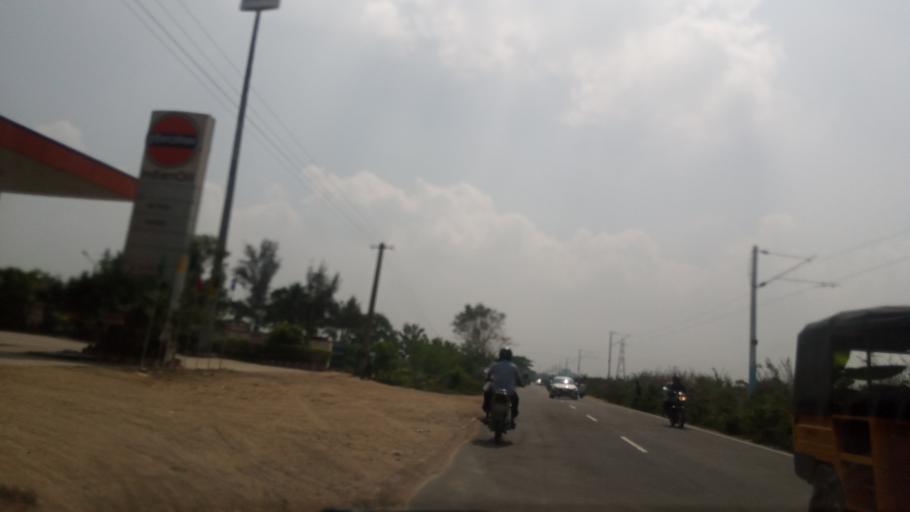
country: IN
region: Tamil Nadu
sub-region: Kancheepuram
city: Kanchipuram
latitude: 12.8917
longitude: 79.6864
